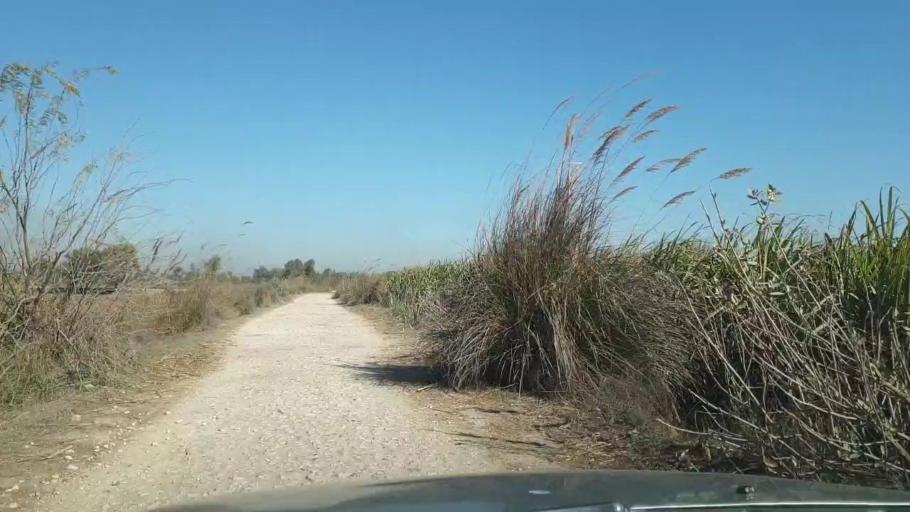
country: PK
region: Sindh
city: Ghotki
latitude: 28.0297
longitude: 69.2880
